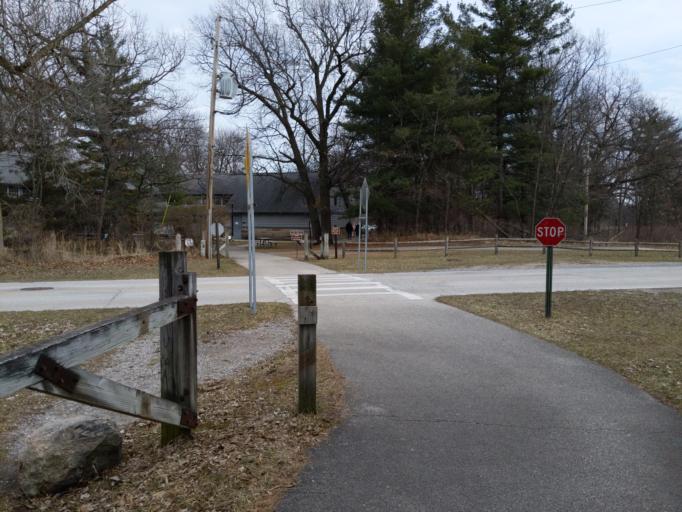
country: US
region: Michigan
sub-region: Bay County
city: Bay City
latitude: 43.6700
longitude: -83.9124
